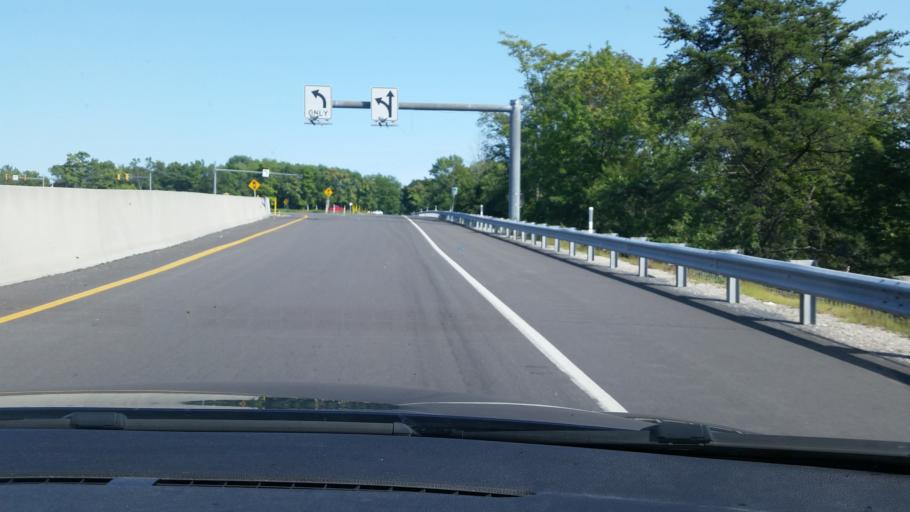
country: US
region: Pennsylvania
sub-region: Berks County
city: West Hamburg
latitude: 40.5555
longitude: -75.9986
